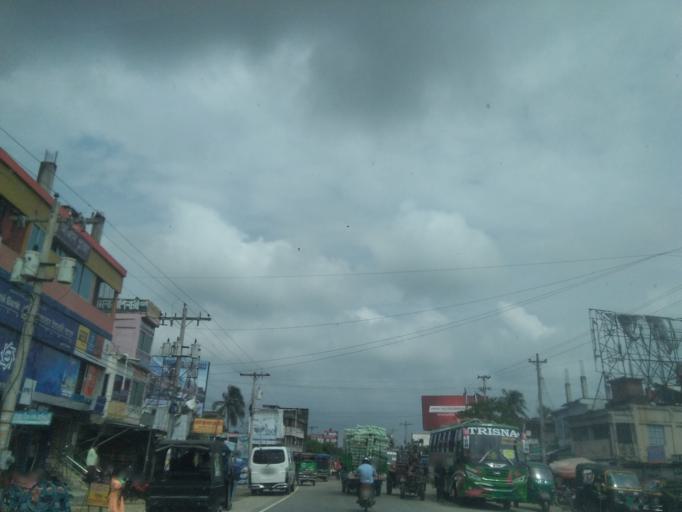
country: BD
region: Khulna
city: Kesabpur
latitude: 22.8404
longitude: 89.2963
